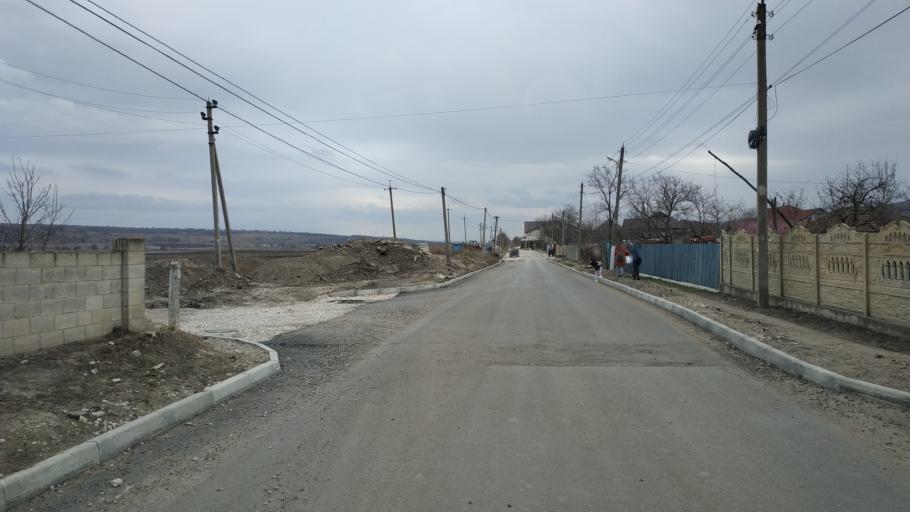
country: MD
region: Laloveni
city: Ialoveni
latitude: 46.8599
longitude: 28.7856
